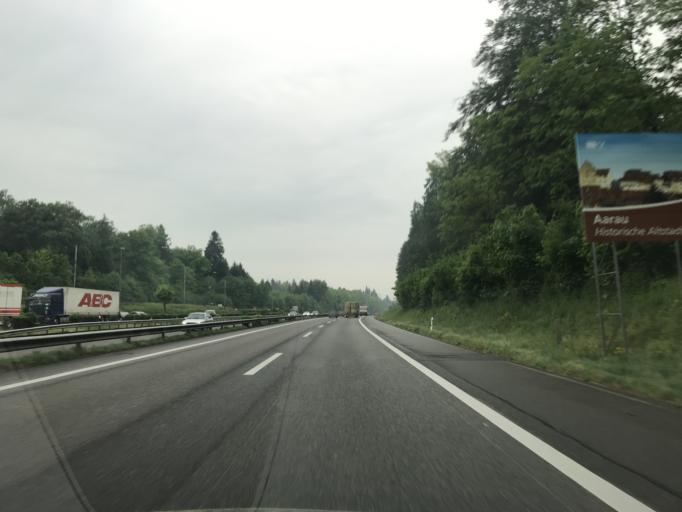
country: CH
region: Aargau
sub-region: Bezirk Lenzburg
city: Staufen
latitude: 47.3933
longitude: 8.1608
